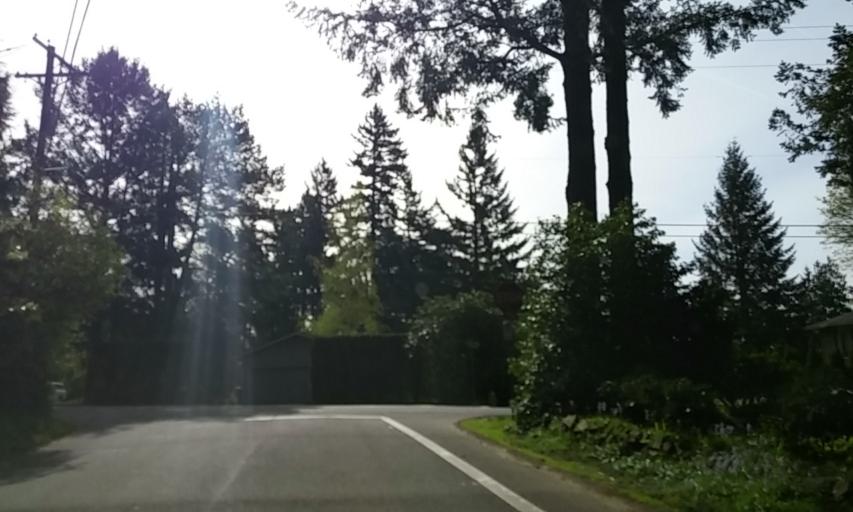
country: US
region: Oregon
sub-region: Washington County
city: West Slope
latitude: 45.5029
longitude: -122.7558
